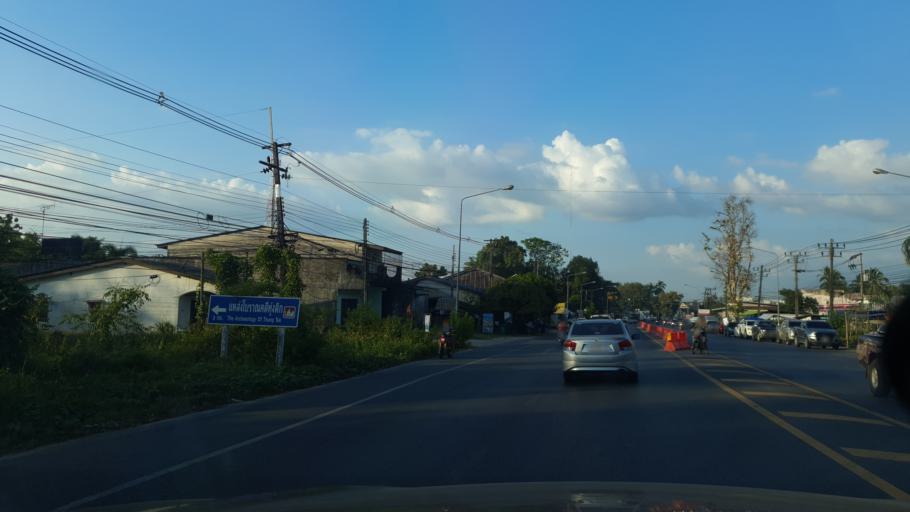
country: TH
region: Phangnga
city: Takua Pa
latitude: 8.8379
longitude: 98.2836
